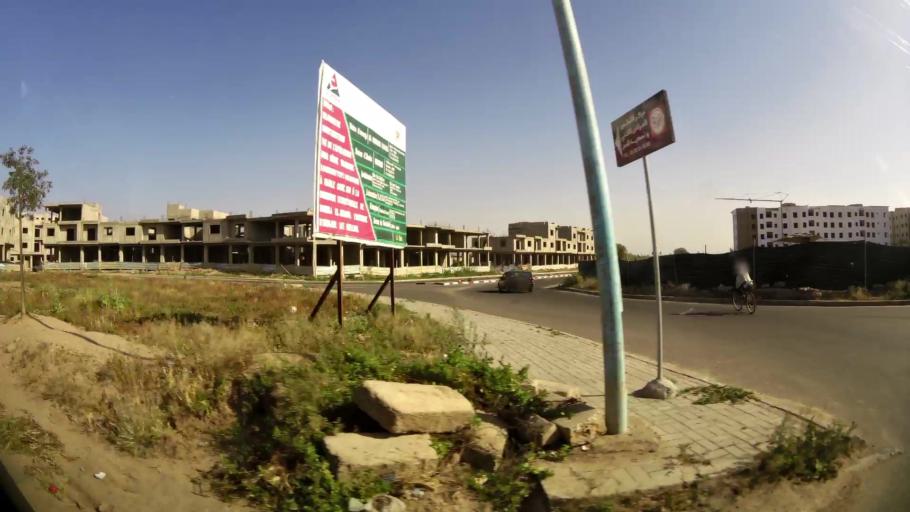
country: MA
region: Souss-Massa-Draa
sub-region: Inezgane-Ait Mellou
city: Inezgane
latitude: 30.3723
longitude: -9.5186
